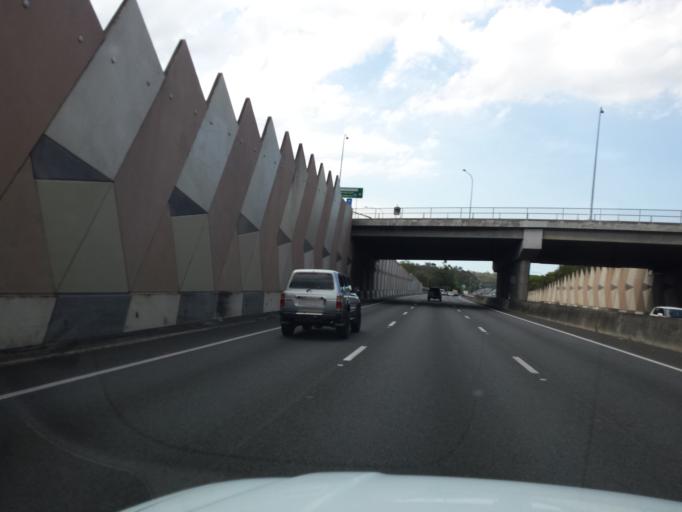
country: AU
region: Queensland
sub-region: Gold Coast
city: Nerang
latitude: -27.9943
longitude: 153.3399
